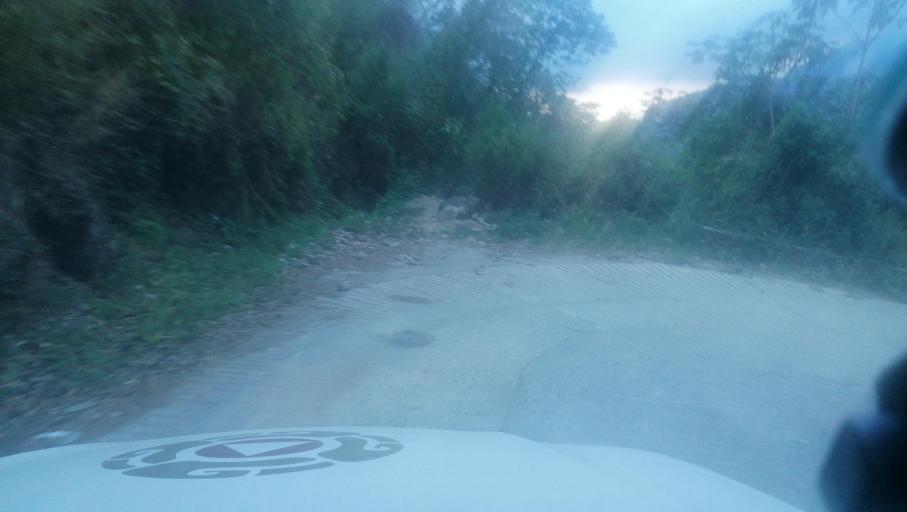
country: MX
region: Chiapas
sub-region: Cacahoatan
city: Benito Juarez
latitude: 15.1397
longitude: -92.1954
